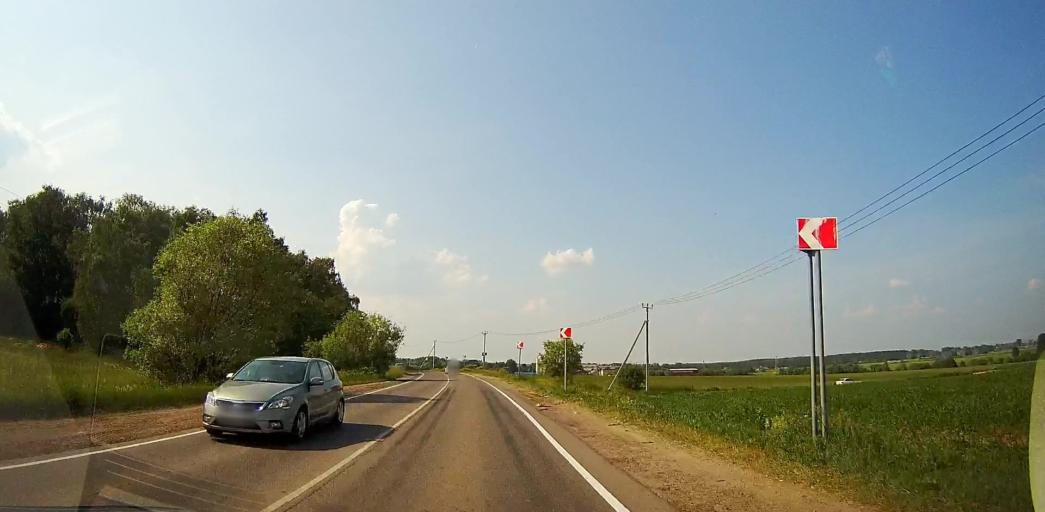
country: RU
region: Moskovskaya
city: Zhitnevo
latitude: 55.3071
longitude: 37.9098
